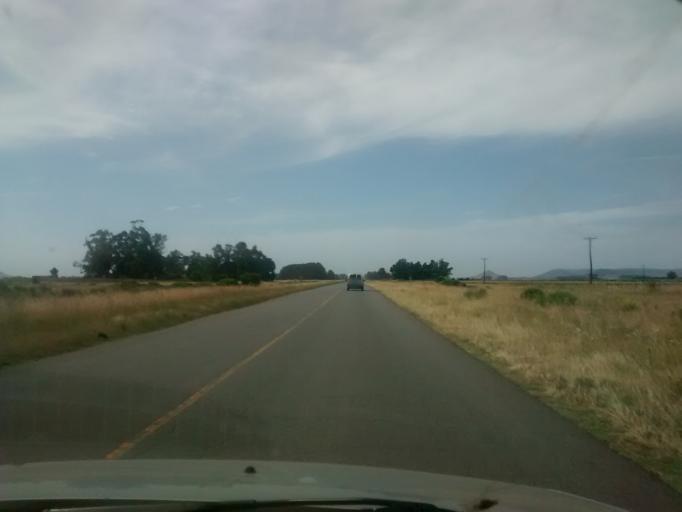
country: AR
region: Buenos Aires
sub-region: Partido de Loberia
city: Loberia
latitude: -37.9717
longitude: -58.6888
